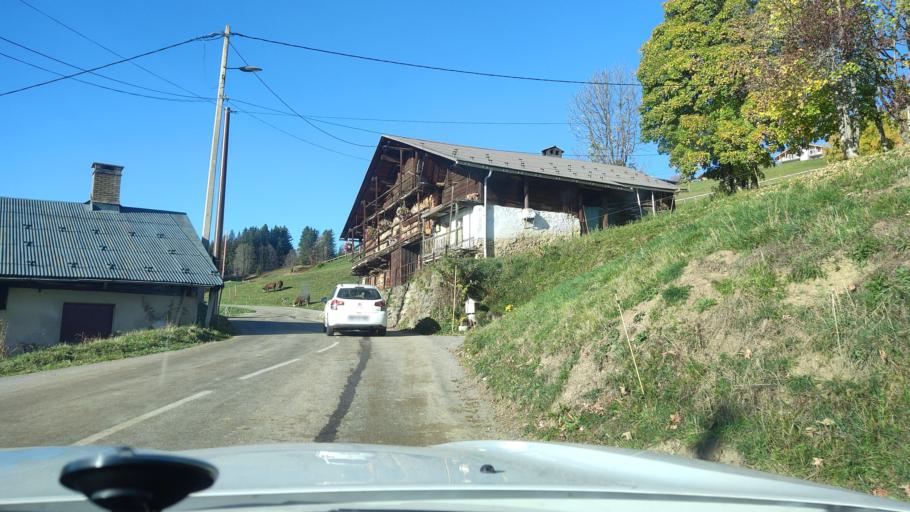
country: FR
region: Rhone-Alpes
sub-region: Departement de la Savoie
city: Beaufort
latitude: 45.7421
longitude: 6.5593
